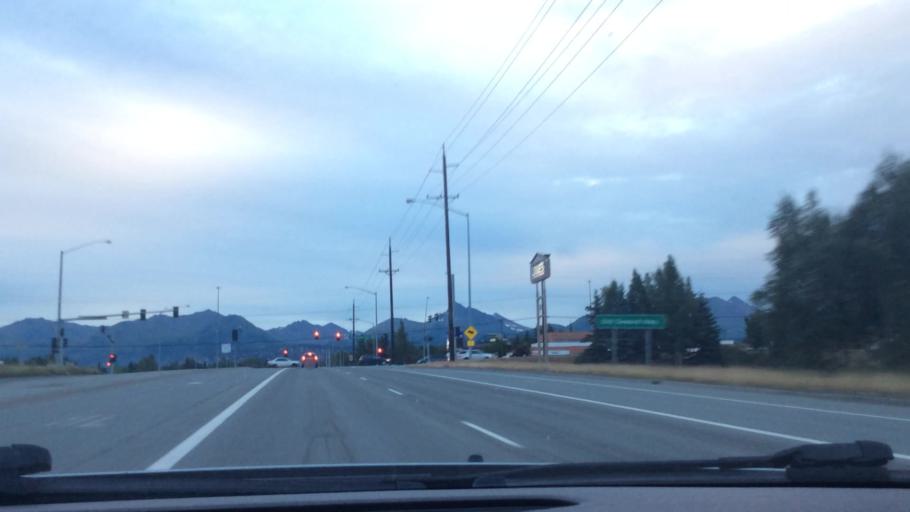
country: US
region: Alaska
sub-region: Anchorage Municipality
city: Anchorage
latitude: 61.1230
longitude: -149.8663
